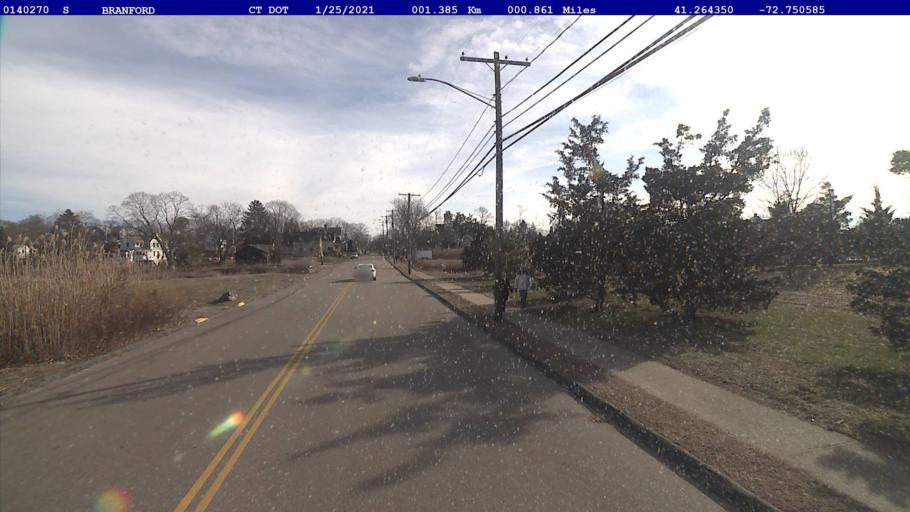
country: US
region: Connecticut
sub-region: New Haven County
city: North Branford
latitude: 41.2643
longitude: -72.7506
